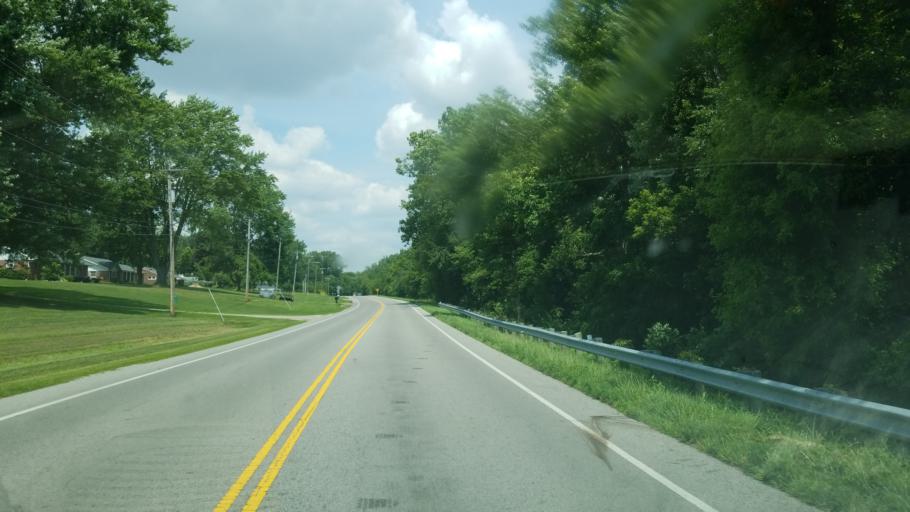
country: US
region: Ohio
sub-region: Henry County
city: Napoleon
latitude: 41.3589
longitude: -84.1516
